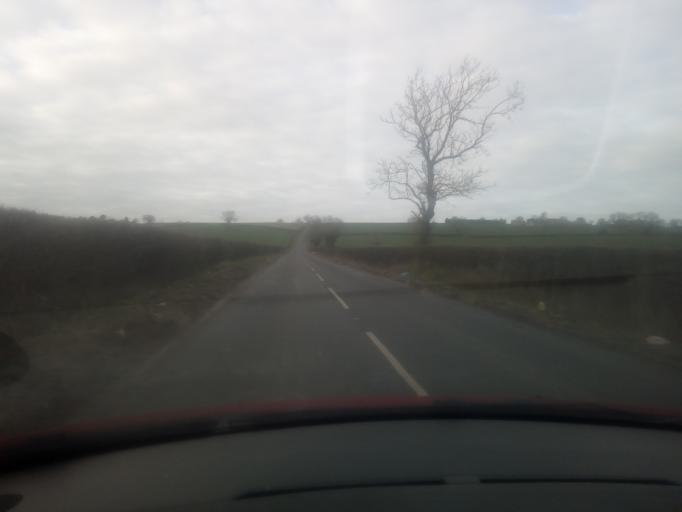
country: GB
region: England
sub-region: Darlington
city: Summerhouse
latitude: 54.5906
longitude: -1.6802
